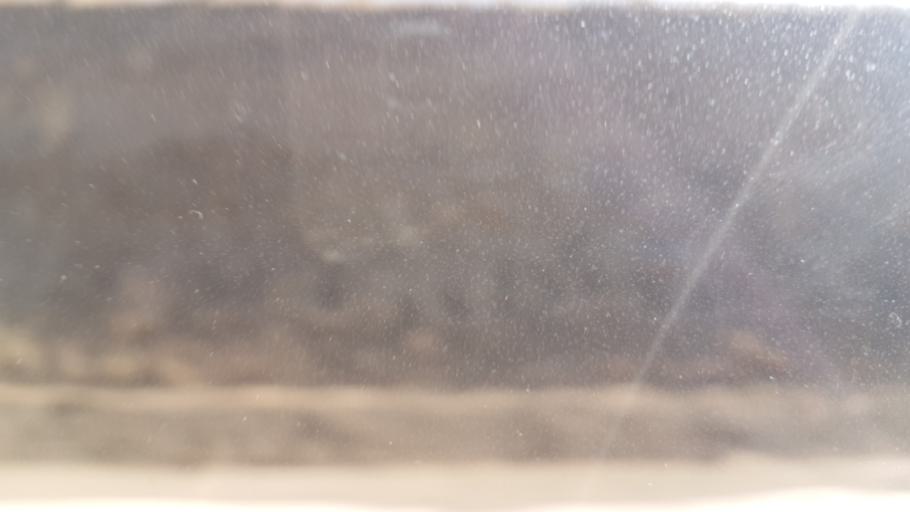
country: TR
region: Ankara
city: Yenice
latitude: 39.3670
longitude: 32.6929
